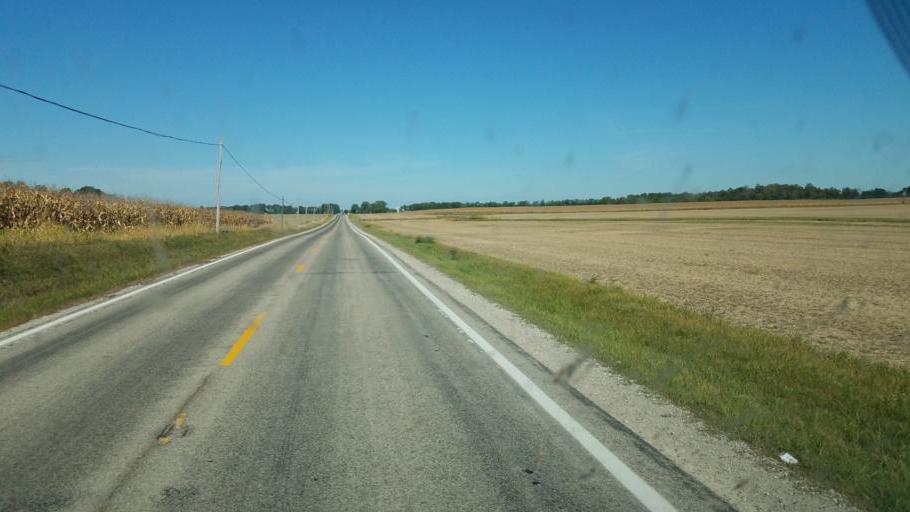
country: US
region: Ohio
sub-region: Crawford County
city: Bucyrus
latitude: 40.9126
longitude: -83.0166
